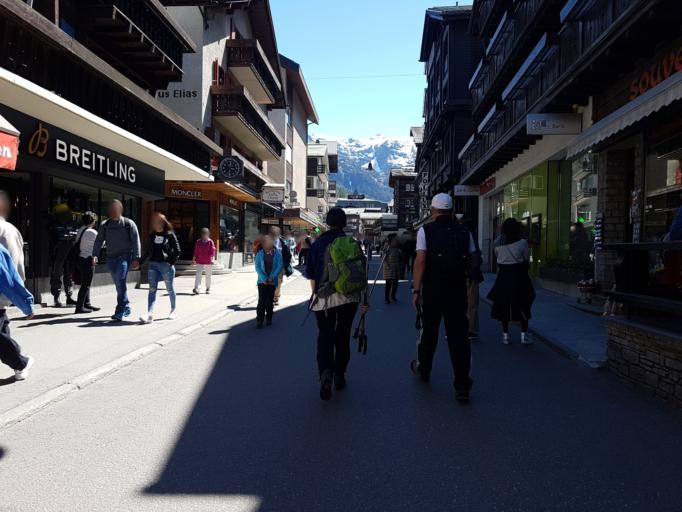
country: CH
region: Valais
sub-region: Visp District
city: Zermatt
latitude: 46.0226
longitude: 7.7474
